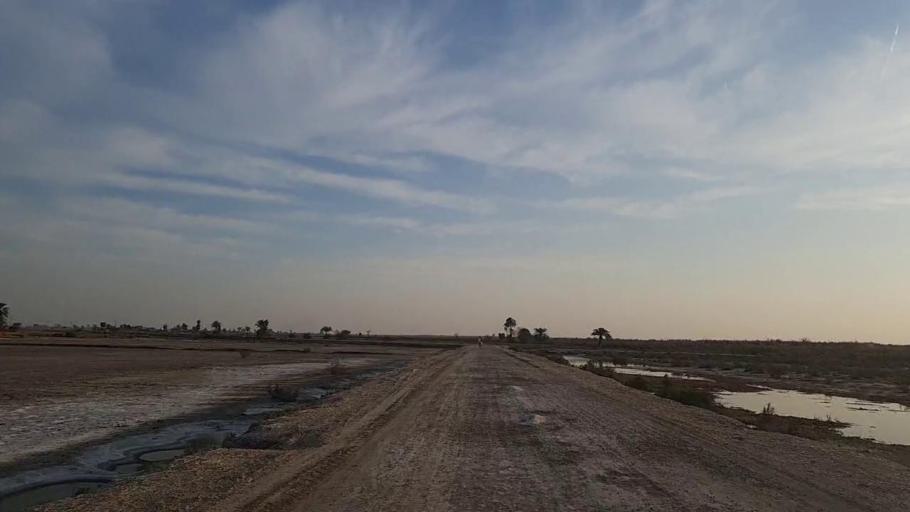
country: PK
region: Sindh
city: Bandhi
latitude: 26.5800
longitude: 68.3336
